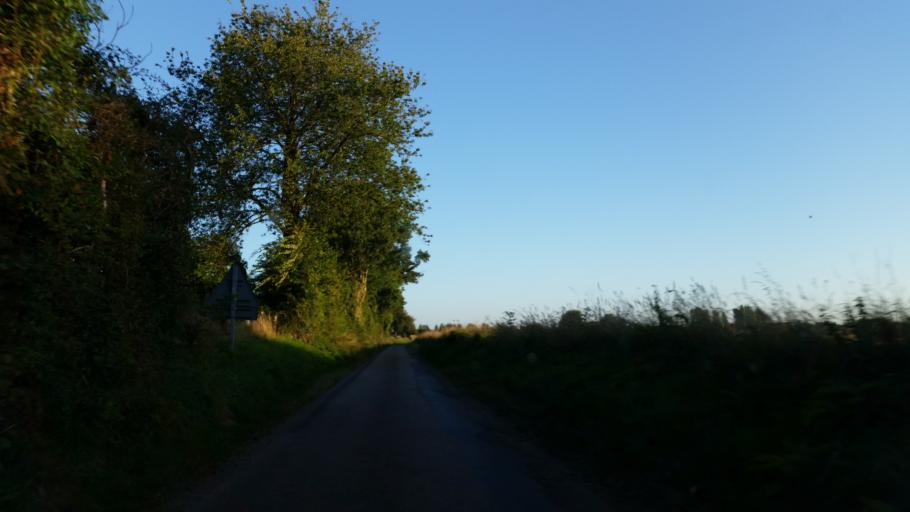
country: FR
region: Lower Normandy
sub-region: Departement du Calvados
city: Equemauville
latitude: 49.3791
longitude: 0.2286
